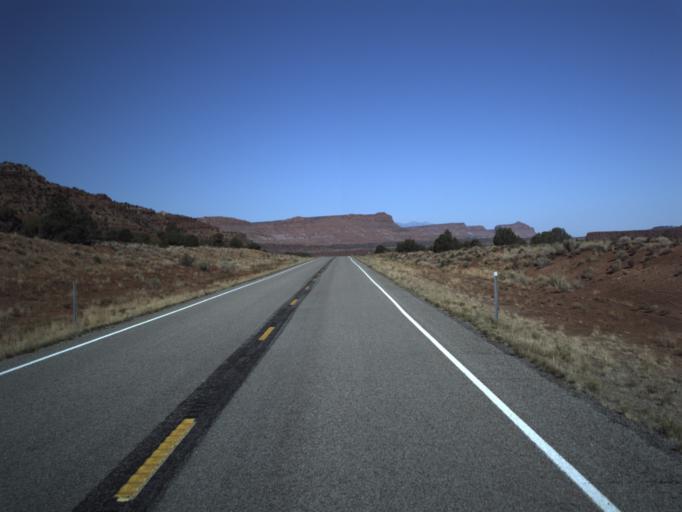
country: US
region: Utah
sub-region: San Juan County
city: Blanding
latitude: 37.6587
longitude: -110.1826
